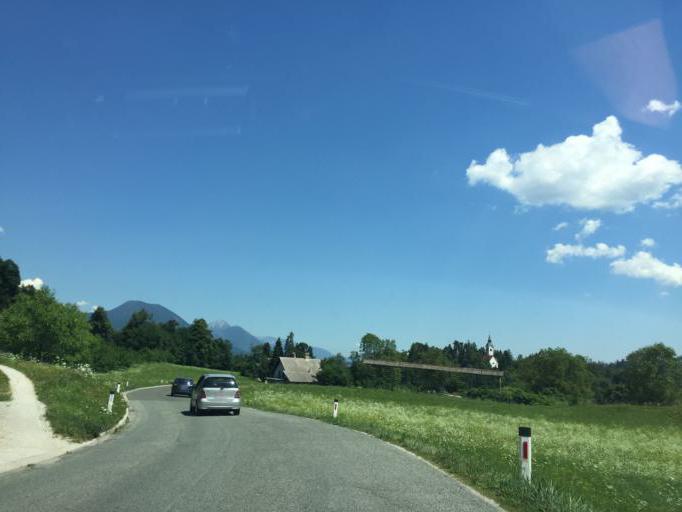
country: SI
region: Gorje
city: Zgornje Gorje
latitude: 46.3820
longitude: 14.0833
